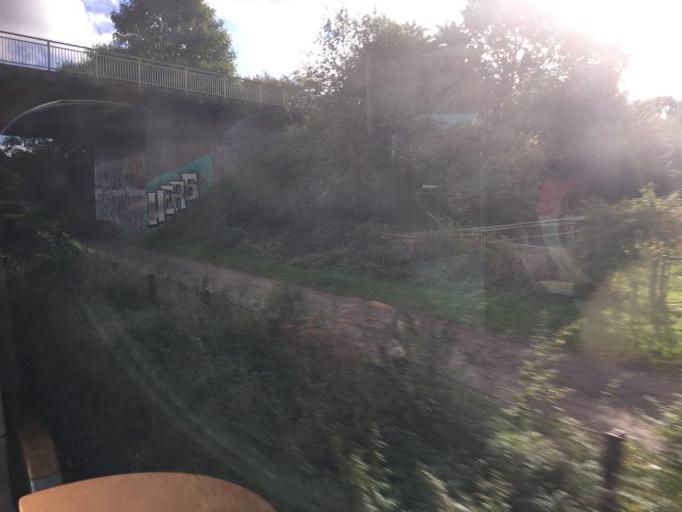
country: DE
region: Schleswig-Holstein
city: Kronshagen
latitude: 54.3105
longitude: 10.0747
